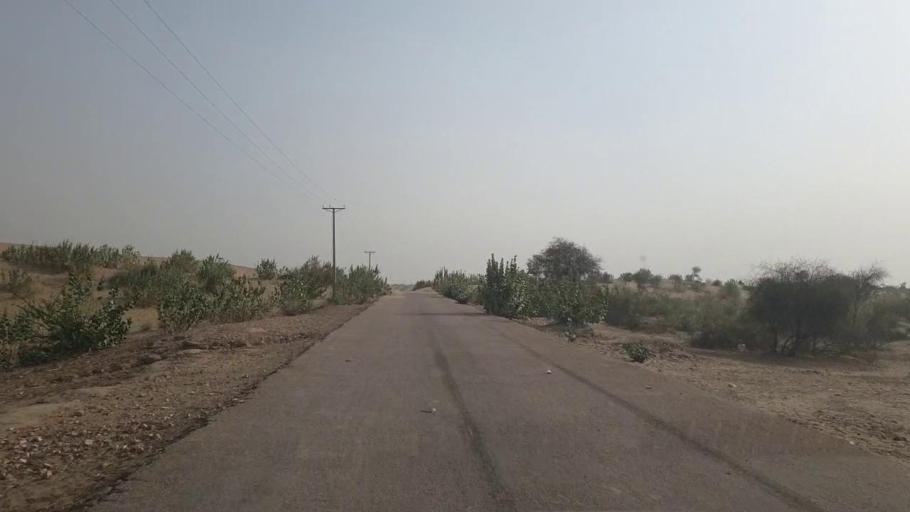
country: PK
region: Sindh
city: Chor
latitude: 25.5372
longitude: 69.9601
